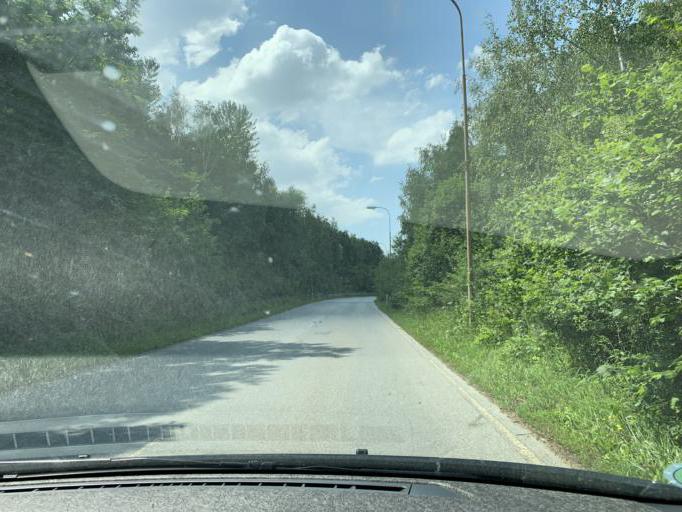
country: DE
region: North Rhine-Westphalia
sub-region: Regierungsbezirk Dusseldorf
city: Grevenbroich
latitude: 51.0520
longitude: 6.5615
